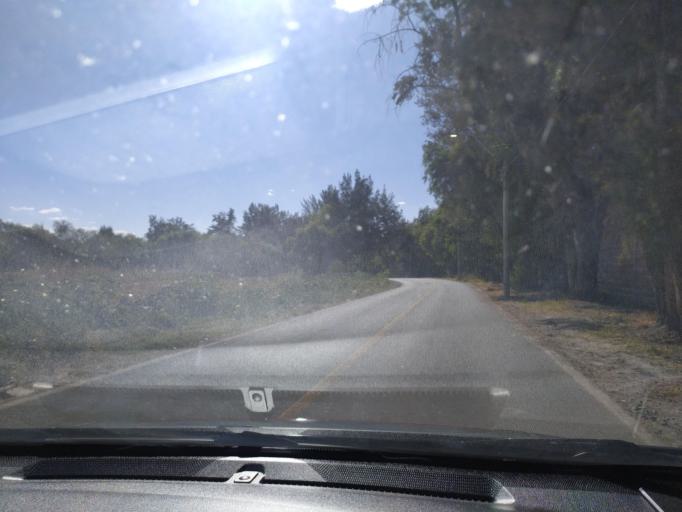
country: LA
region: Oudomxai
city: Muang La
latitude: 21.0438
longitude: 101.8359
